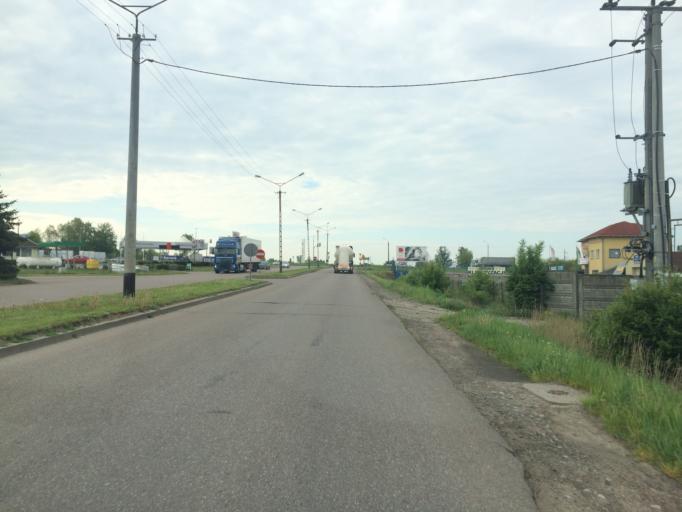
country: PL
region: Masovian Voivodeship
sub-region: Powiat mlawski
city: Mlawa
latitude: 53.0951
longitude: 20.3736
